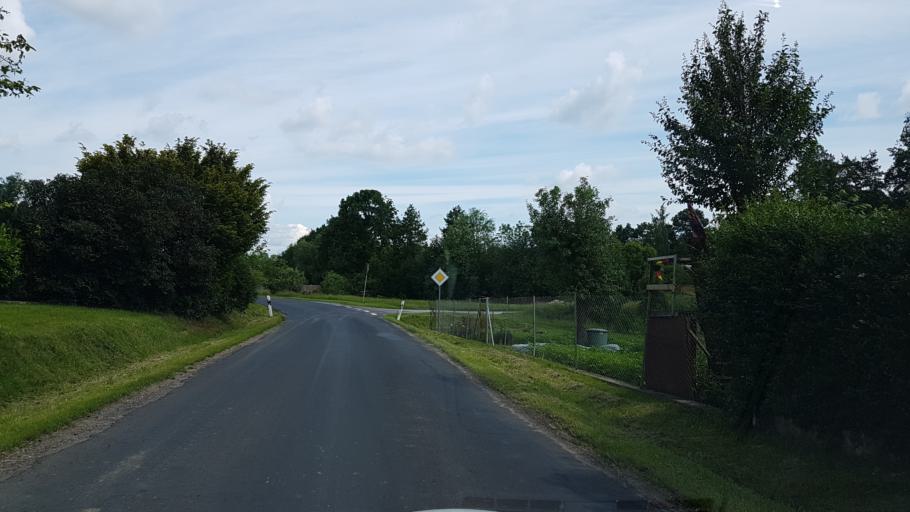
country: DE
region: Bavaria
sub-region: Regierungsbezirk Unterfranken
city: Prichsenstadt
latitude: 49.8380
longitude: 10.3294
